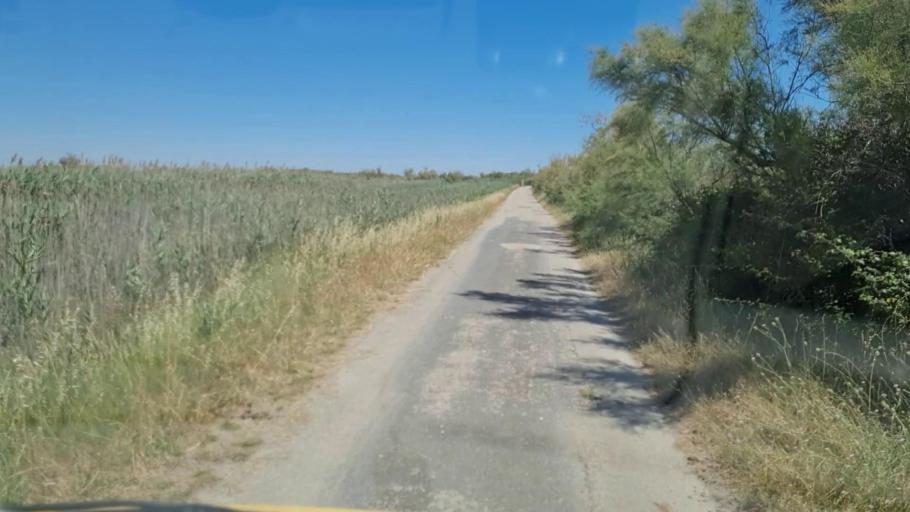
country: FR
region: Languedoc-Roussillon
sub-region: Departement du Gard
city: Le Cailar
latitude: 43.6152
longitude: 4.2642
